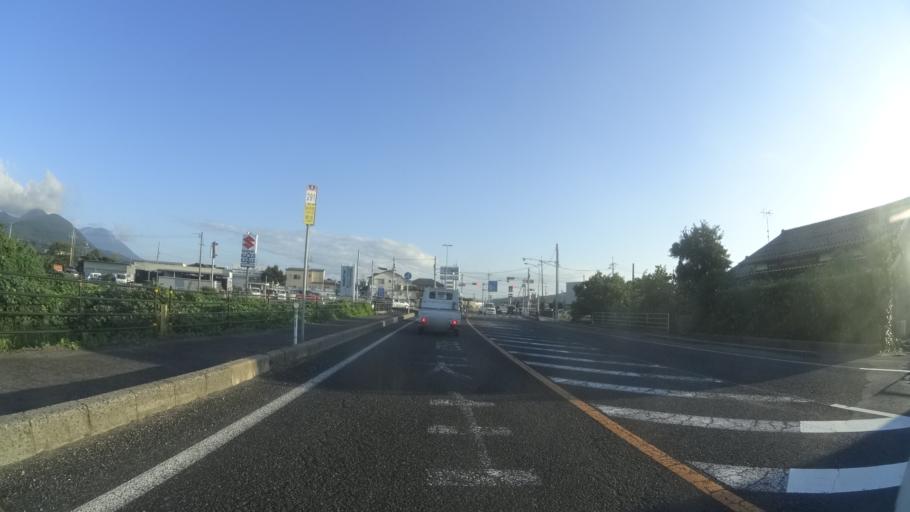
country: JP
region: Tottori
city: Yonago
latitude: 35.4677
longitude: 133.4322
